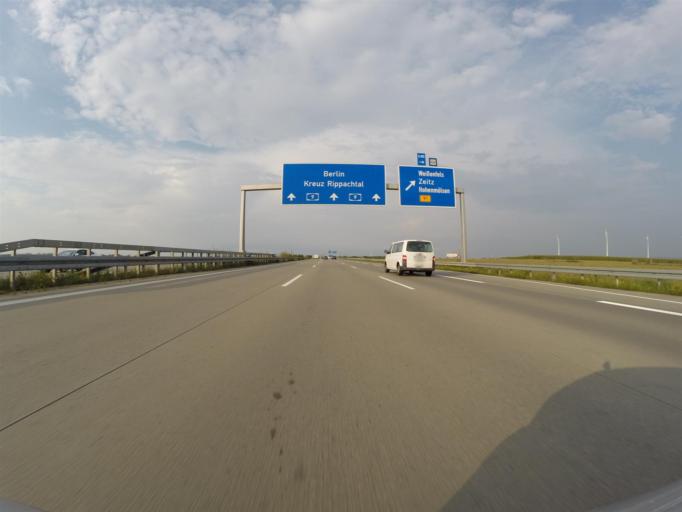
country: DE
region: Saxony-Anhalt
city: Nessa
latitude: 51.1710
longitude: 11.9991
